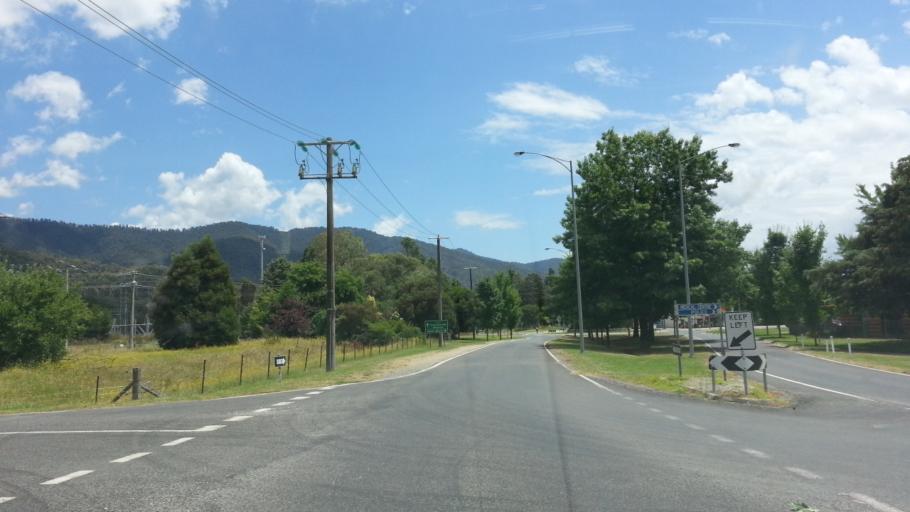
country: AU
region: Victoria
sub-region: Alpine
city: Mount Beauty
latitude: -36.7443
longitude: 147.1691
